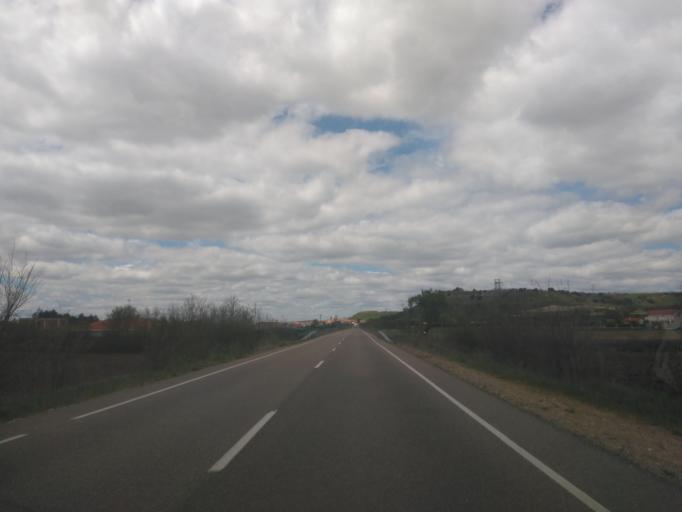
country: ES
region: Castille and Leon
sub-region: Provincia de Salamanca
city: Almenara de Tormes
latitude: 41.0573
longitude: -5.8034
